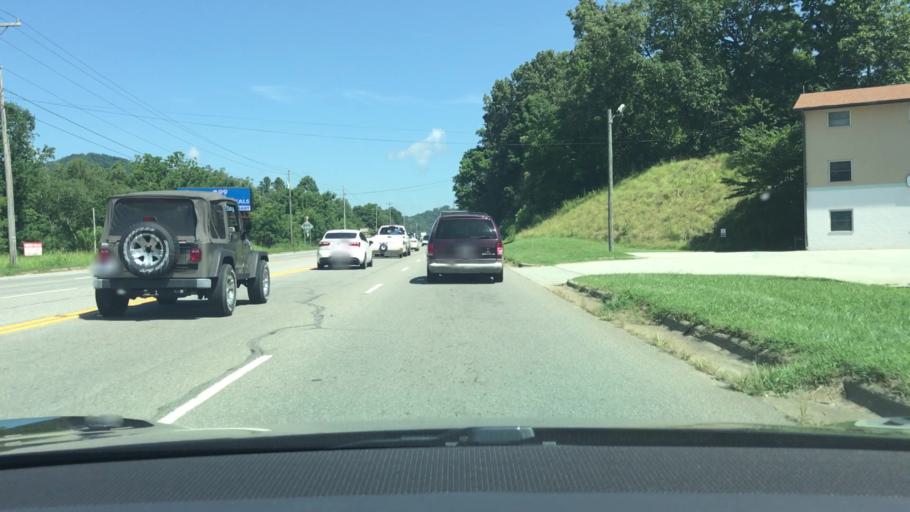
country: US
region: North Carolina
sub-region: Macon County
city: Franklin
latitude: 35.1216
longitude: -83.3928
